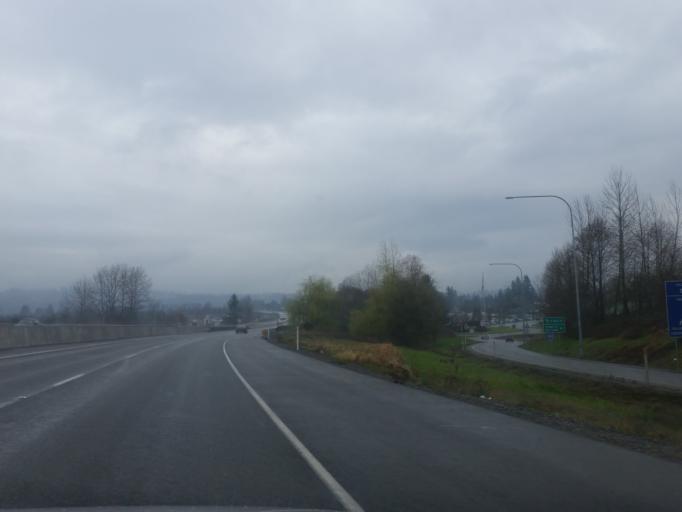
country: US
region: Washington
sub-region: Snohomish County
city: Monroe
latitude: 47.8477
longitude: -122.0093
